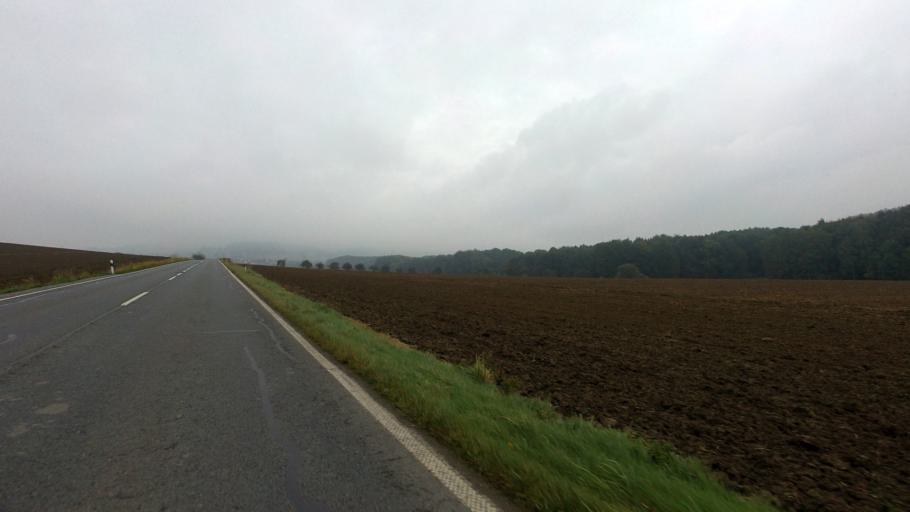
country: DE
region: Saxony
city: Neustadt in Sachsen
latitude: 51.0128
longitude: 14.2322
